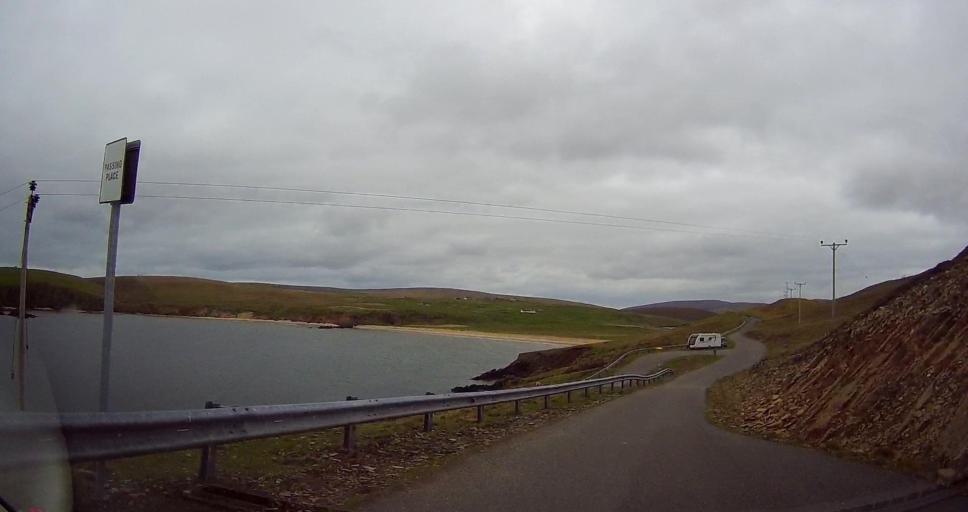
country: GB
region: Scotland
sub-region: Shetland Islands
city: Shetland
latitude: 60.8113
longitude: -0.8768
